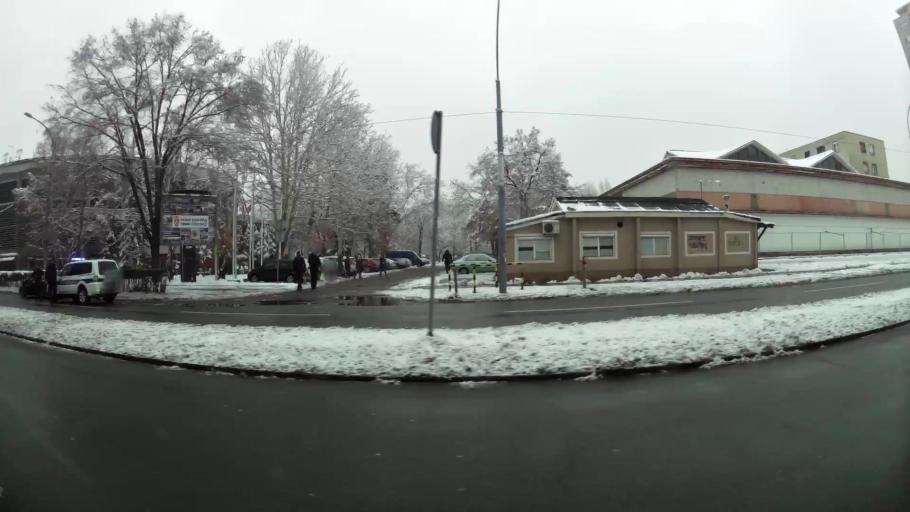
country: RS
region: Central Serbia
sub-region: Belgrade
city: Zemun
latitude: 44.8275
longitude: 20.4077
